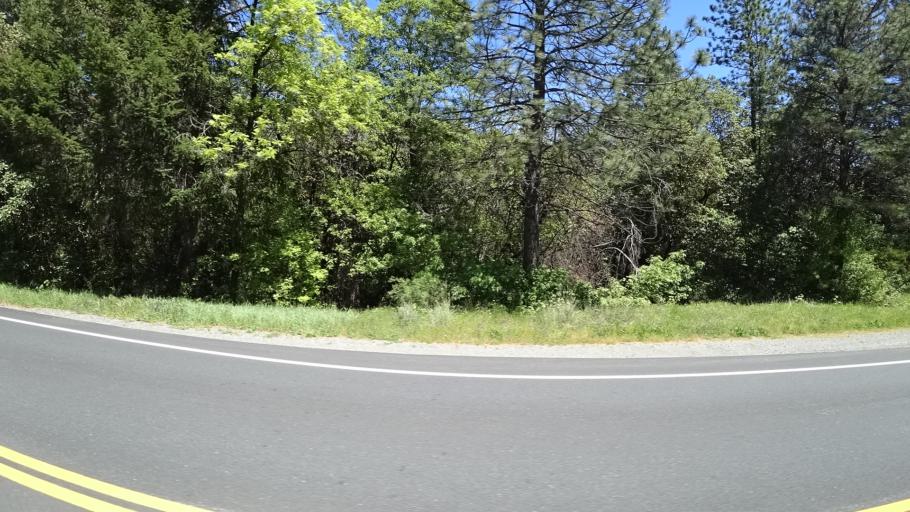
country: US
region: California
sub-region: Humboldt County
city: Willow Creek
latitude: 40.8082
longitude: -123.4739
